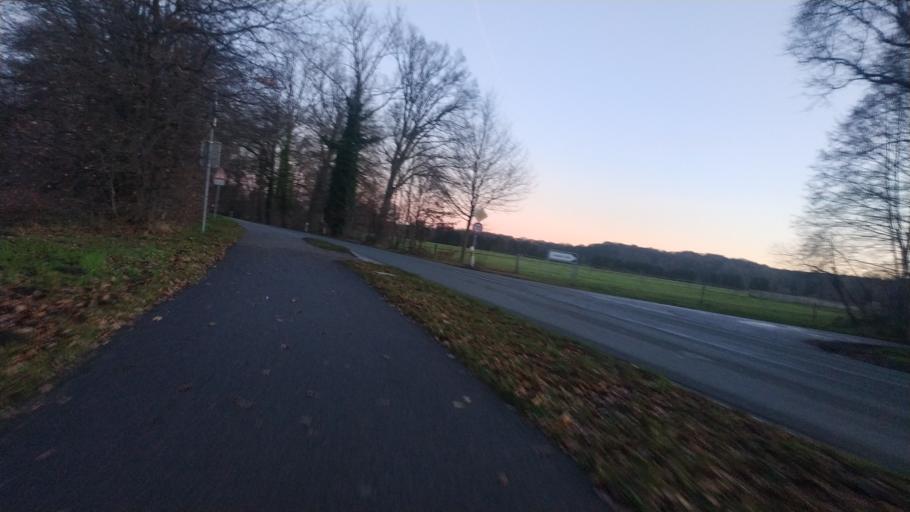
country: DE
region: North Rhine-Westphalia
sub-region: Regierungsbezirk Munster
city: Birgte
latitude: 52.2755
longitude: 7.6662
